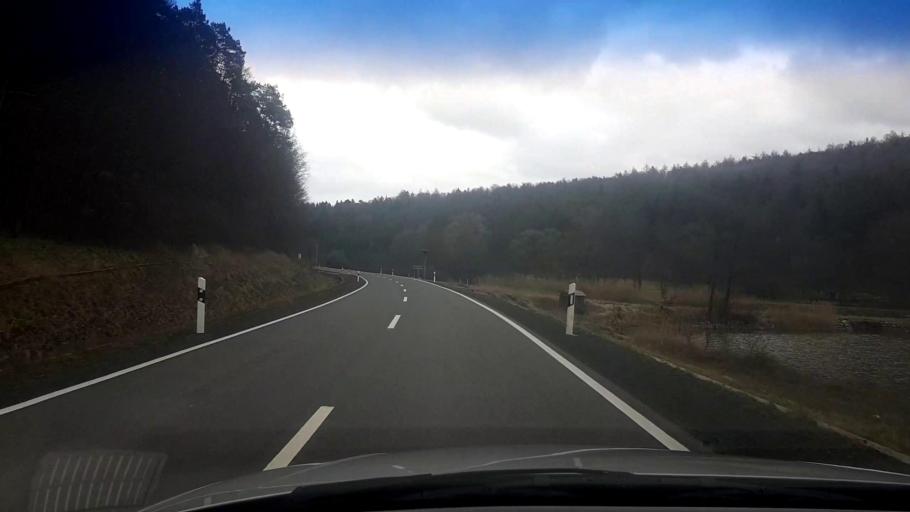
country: DE
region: Bavaria
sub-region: Regierungsbezirk Unterfranken
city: Eltmann
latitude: 49.9361
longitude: 10.6280
